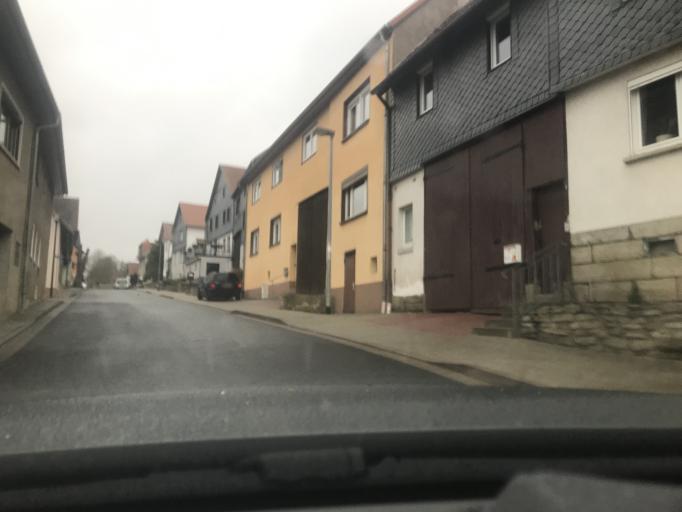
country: DE
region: Thuringia
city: Heyerode
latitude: 51.2105
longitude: 10.3260
